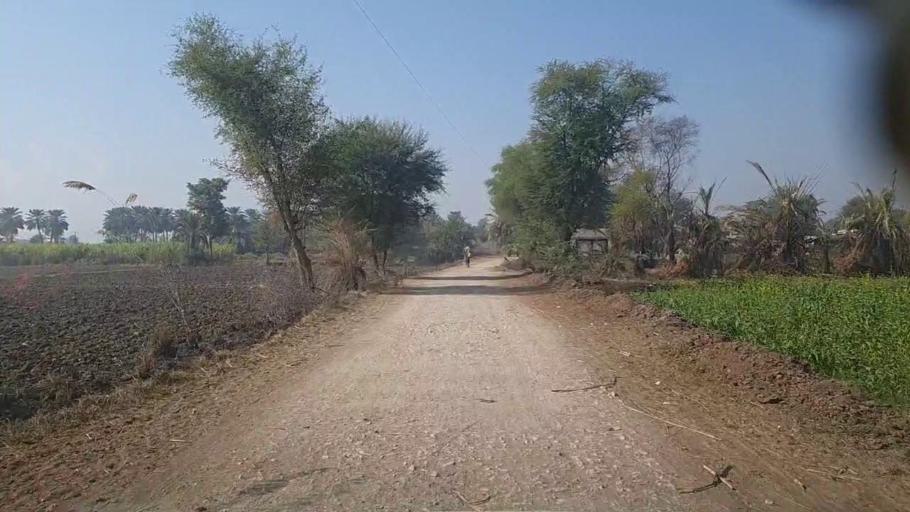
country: PK
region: Sindh
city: Kandiari
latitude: 26.9942
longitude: 68.4754
